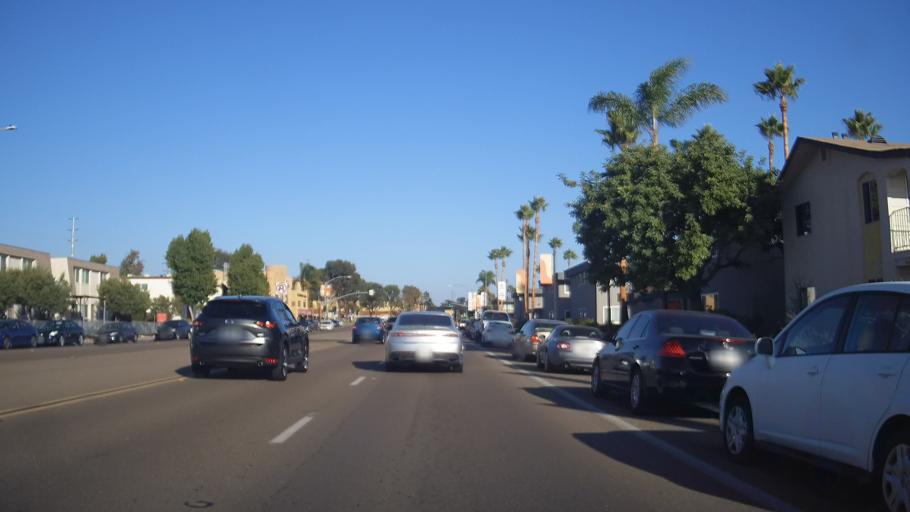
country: US
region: California
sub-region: San Diego County
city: La Jolla
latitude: 32.8343
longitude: -117.1776
